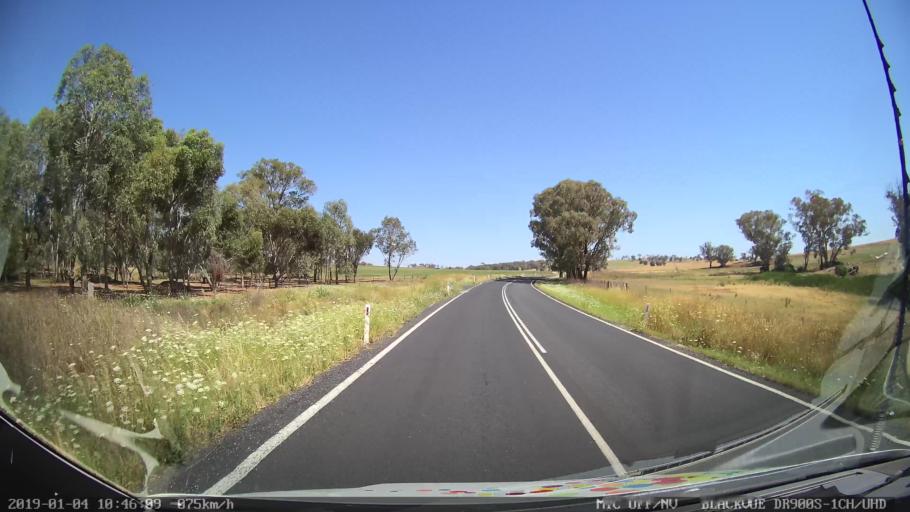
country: AU
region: New South Wales
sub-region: Cabonne
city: Molong
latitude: -33.2842
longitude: 148.7246
